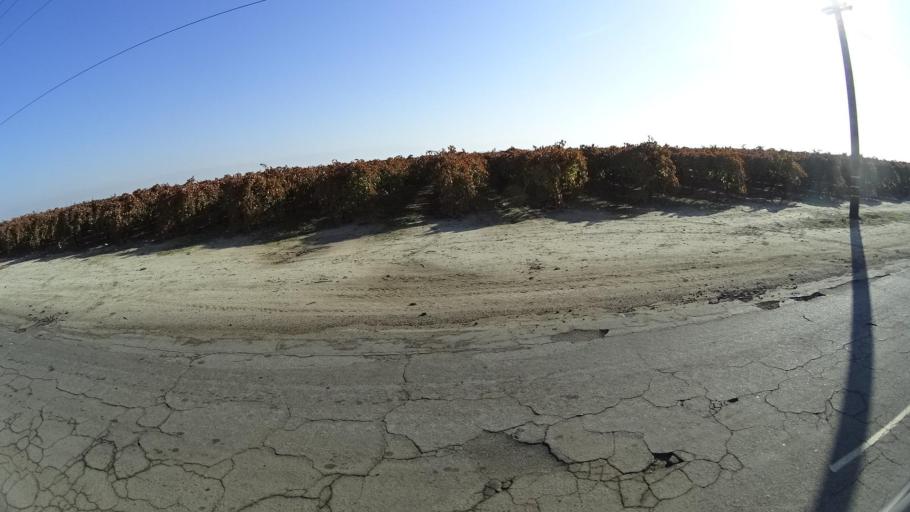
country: US
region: California
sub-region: Kern County
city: McFarland
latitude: 35.7278
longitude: -119.1695
